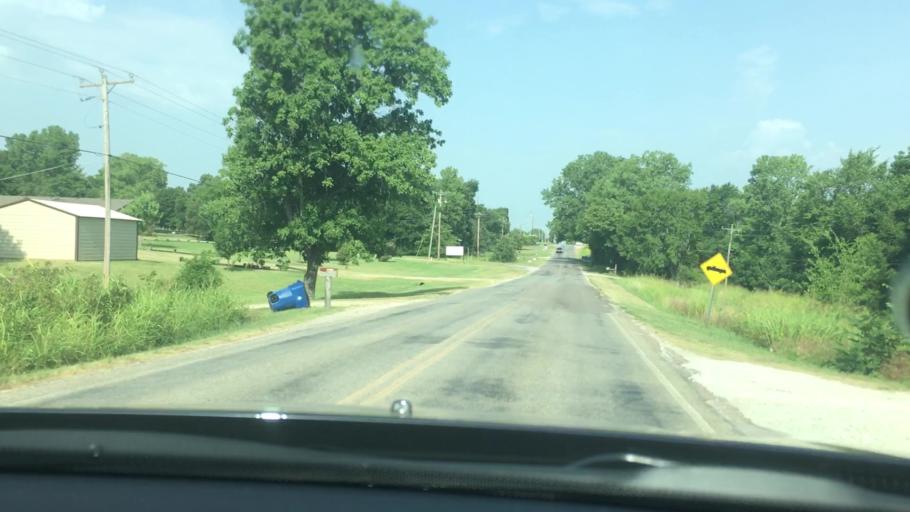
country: US
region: Oklahoma
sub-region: Pontotoc County
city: Byng
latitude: 34.8685
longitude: -96.6624
